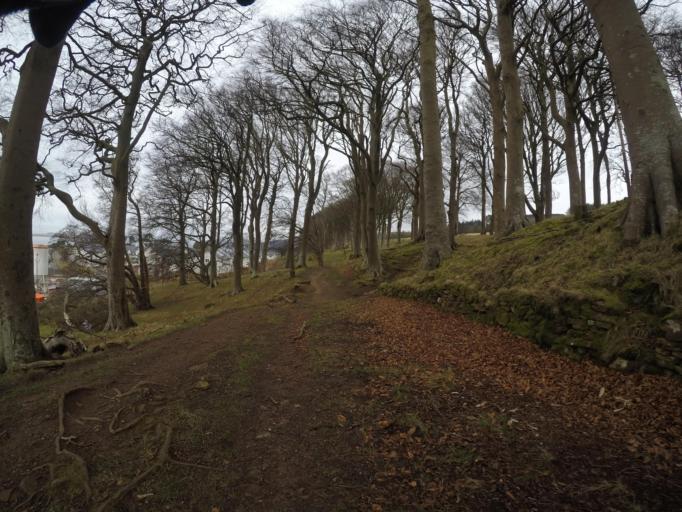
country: GB
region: Scotland
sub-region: North Ayrshire
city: Fairlie
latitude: 55.7574
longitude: -4.8498
